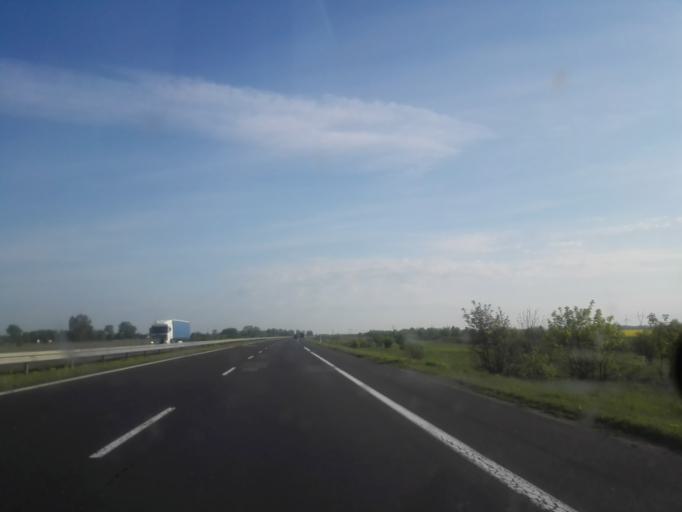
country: PL
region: Lodz Voivodeship
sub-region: Powiat radomszczanski
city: Kamiensk
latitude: 51.2712
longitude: 19.5317
